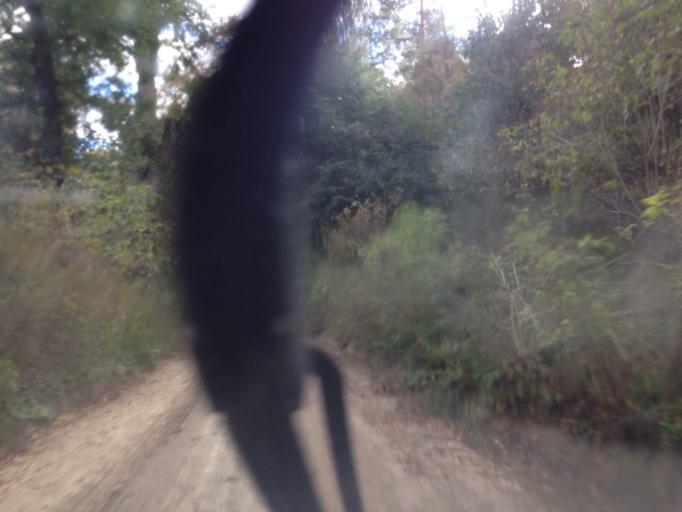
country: PL
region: Warmian-Masurian Voivodeship
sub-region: Powiat ilawski
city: Susz
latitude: 53.7511
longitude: 19.3071
